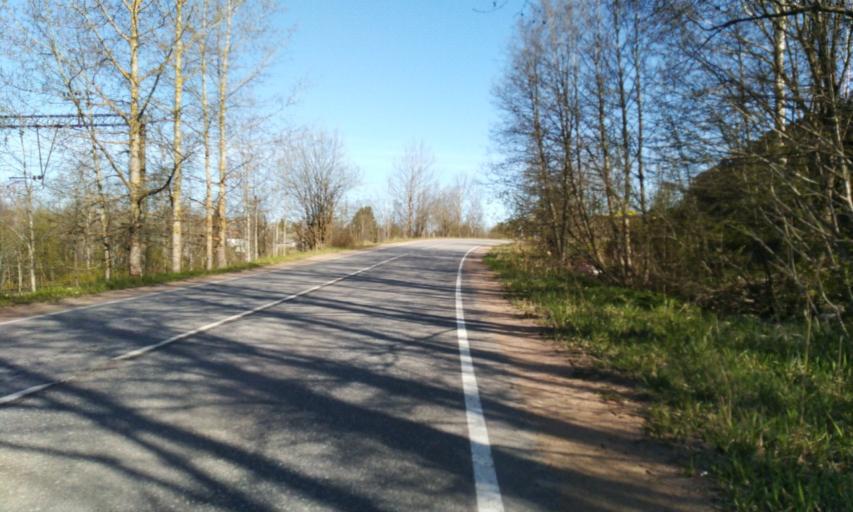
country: RU
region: Leningrad
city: Leskolovo
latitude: 60.3277
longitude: 30.4248
